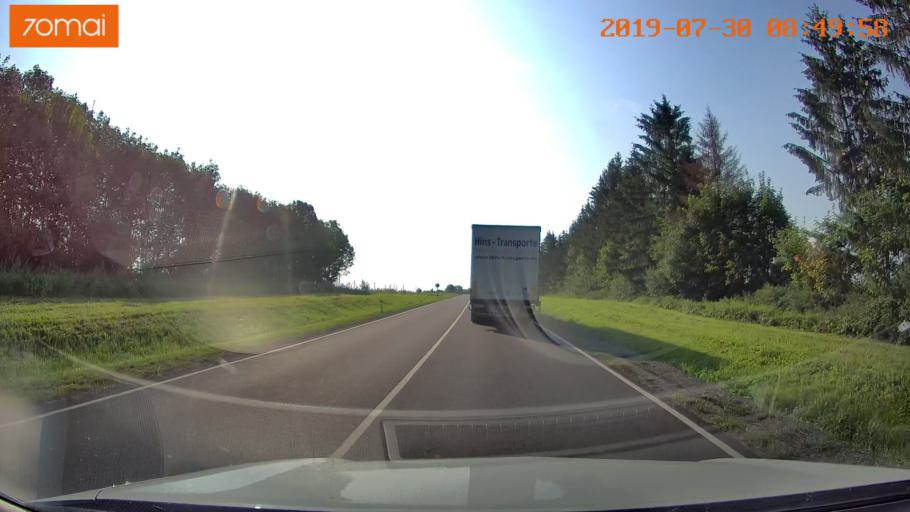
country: RU
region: Kaliningrad
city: Chernyakhovsk
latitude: 54.6101
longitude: 21.9312
